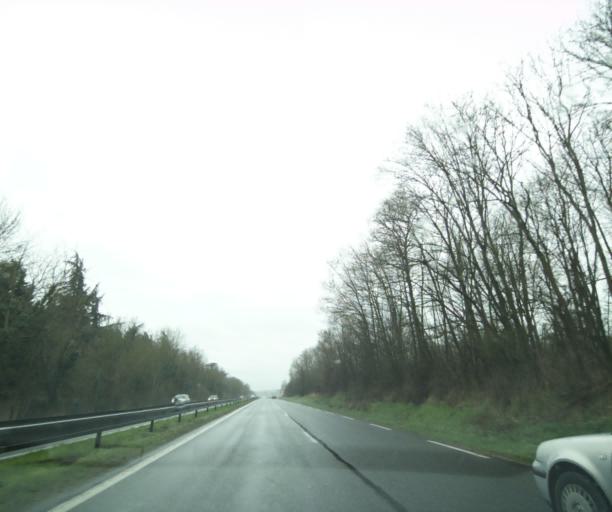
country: FR
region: Ile-de-France
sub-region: Departement de l'Essonne
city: Etrechy
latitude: 48.4717
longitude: 2.1864
